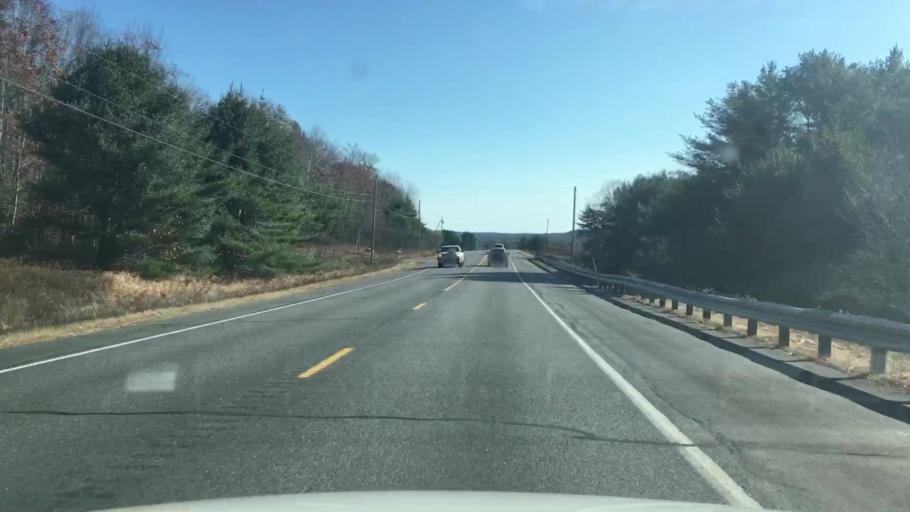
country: US
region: Maine
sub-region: Knox County
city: Union
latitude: 44.2189
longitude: -69.3168
